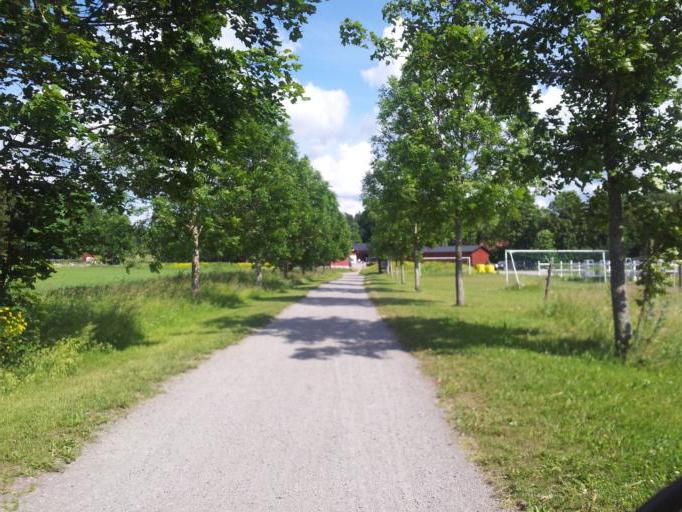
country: SE
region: Uppsala
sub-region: Uppsala Kommun
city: Uppsala
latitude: 59.8802
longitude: 17.6657
